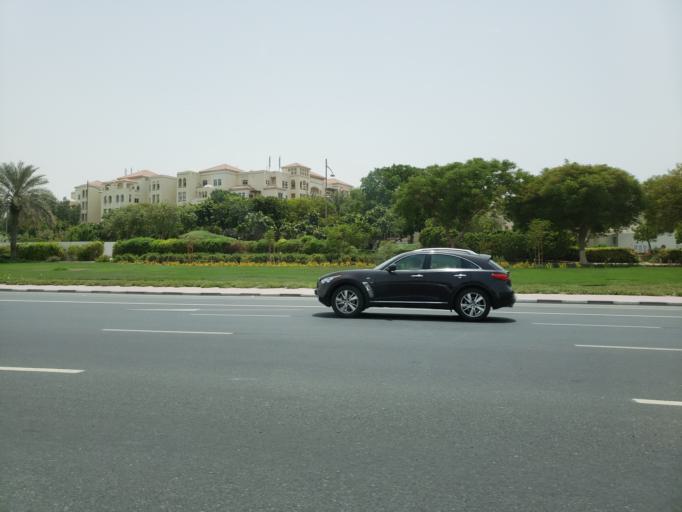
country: AE
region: Ash Shariqah
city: Sharjah
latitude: 25.2206
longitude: 55.3696
